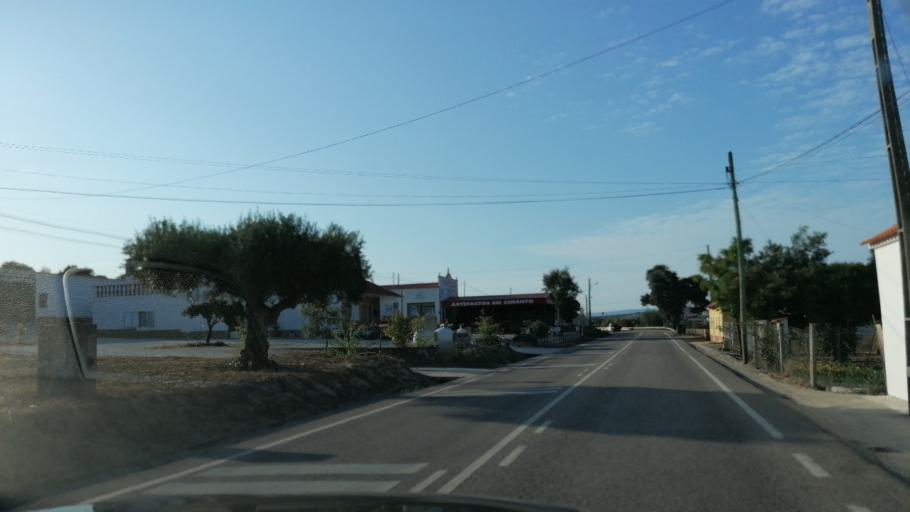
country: PT
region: Santarem
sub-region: Alcanena
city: Alcanena
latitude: 39.3641
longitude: -8.6542
